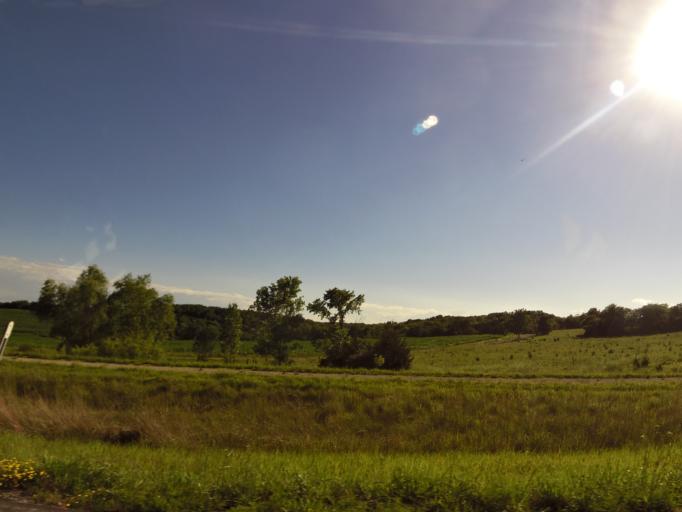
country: US
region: Missouri
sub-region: Pike County
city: Bowling Green
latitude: 39.4621
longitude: -91.2774
